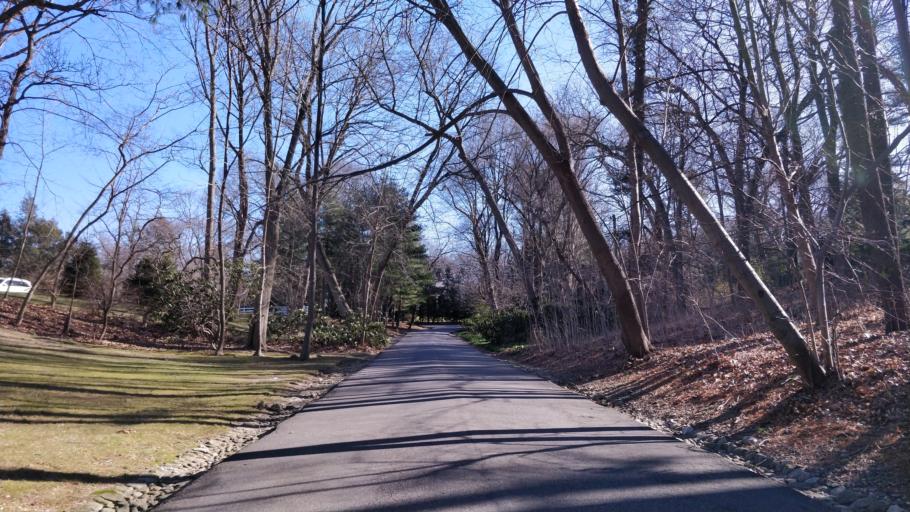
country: US
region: New York
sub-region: Nassau County
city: Brookville
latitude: 40.8202
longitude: -73.5651
